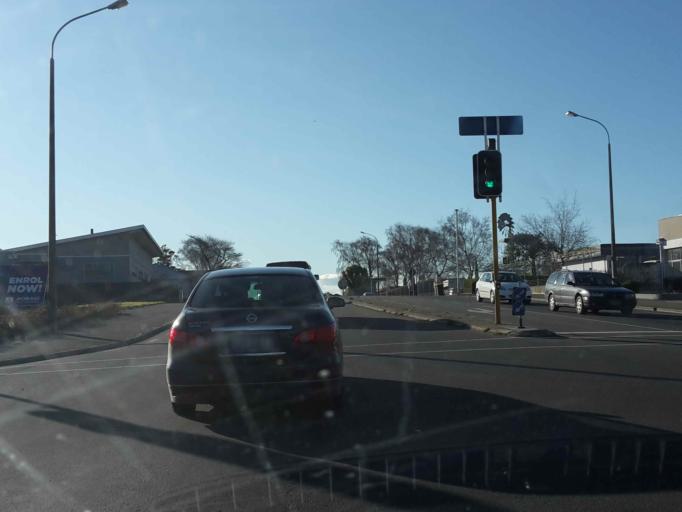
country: NZ
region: Canterbury
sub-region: Timaru District
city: Timaru
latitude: -44.4006
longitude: 171.2485
